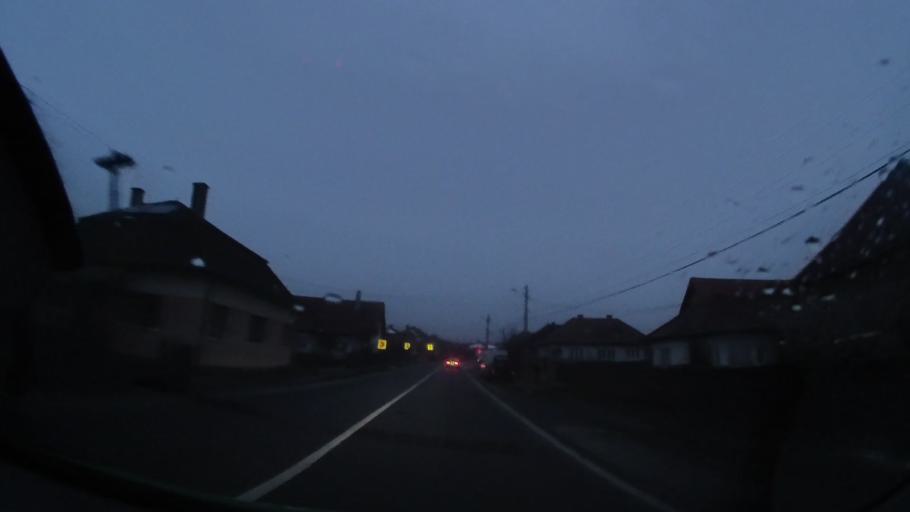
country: RO
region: Harghita
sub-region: Comuna Ditrau
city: Ditrau
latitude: 46.8077
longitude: 25.4929
